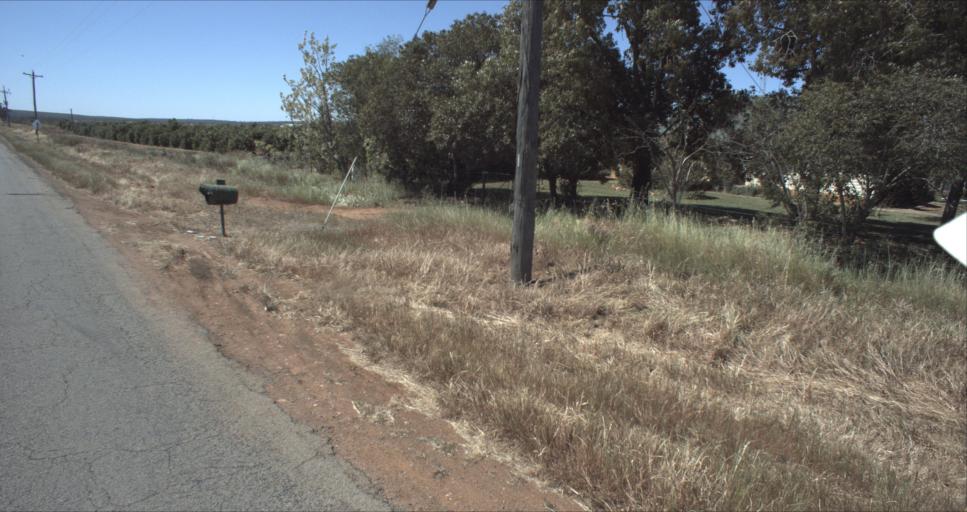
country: AU
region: New South Wales
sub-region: Leeton
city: Leeton
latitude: -34.4798
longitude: 146.4154
